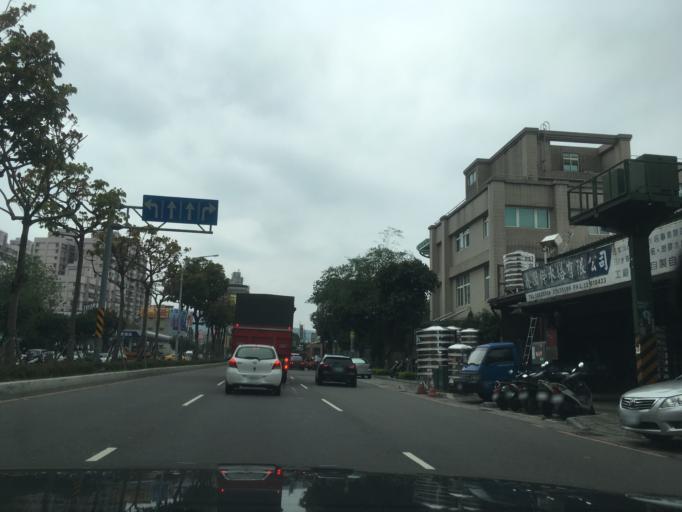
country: TW
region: Taipei
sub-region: Taipei
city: Banqiao
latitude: 24.9805
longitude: 121.4402
